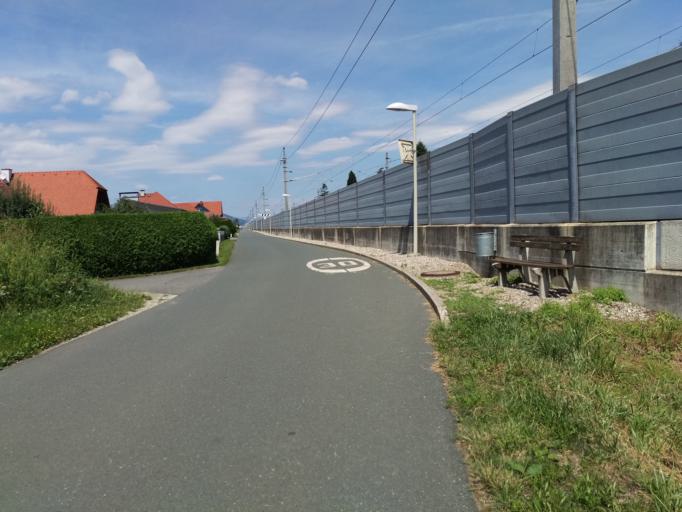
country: AT
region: Styria
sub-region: Politischer Bezirk Graz-Umgebung
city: Gossendorf
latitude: 46.9880
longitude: 15.4554
